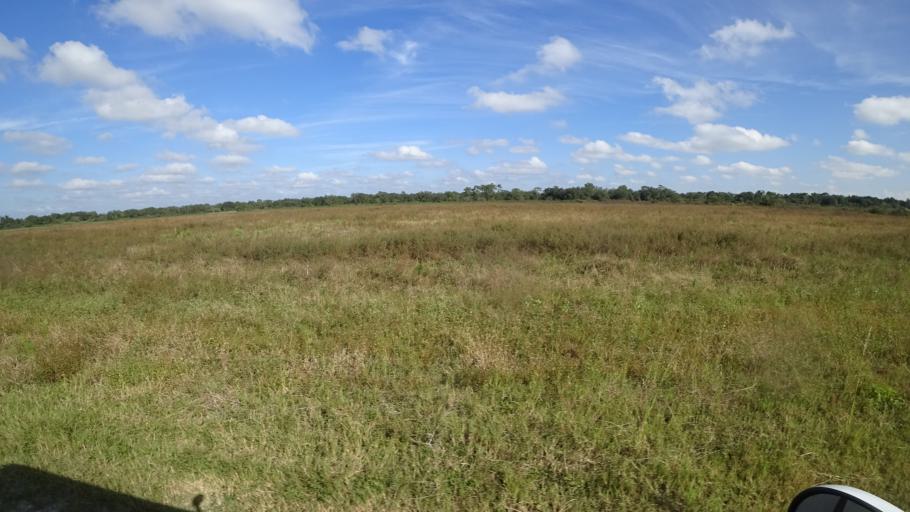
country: US
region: Florida
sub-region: Sarasota County
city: Lake Sarasota
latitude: 27.3685
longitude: -82.1574
